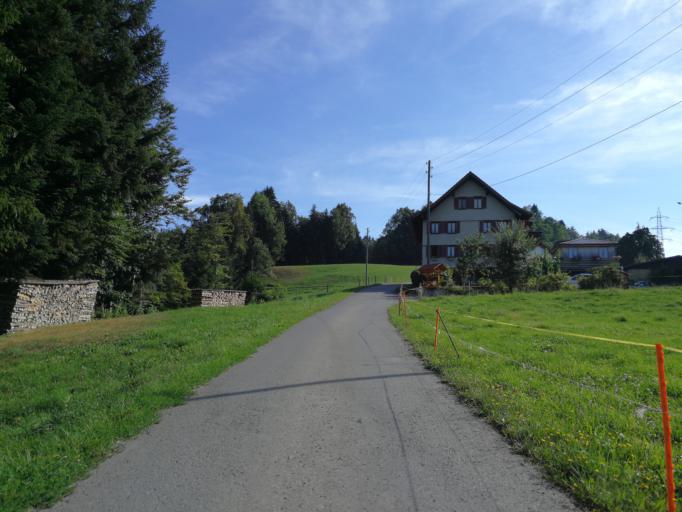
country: CH
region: Saint Gallen
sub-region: Wahlkreis See-Gaster
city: Gommiswald
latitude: 47.2477
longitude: 9.0186
